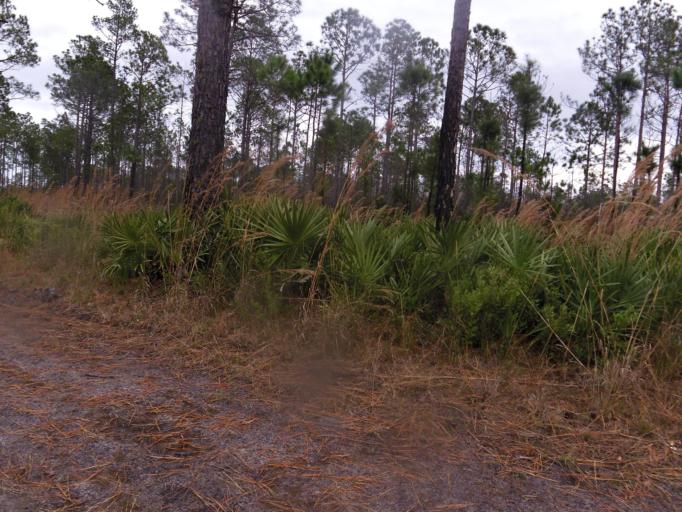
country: US
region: Florida
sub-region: Duval County
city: Atlantic Beach
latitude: 30.4725
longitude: -81.5092
